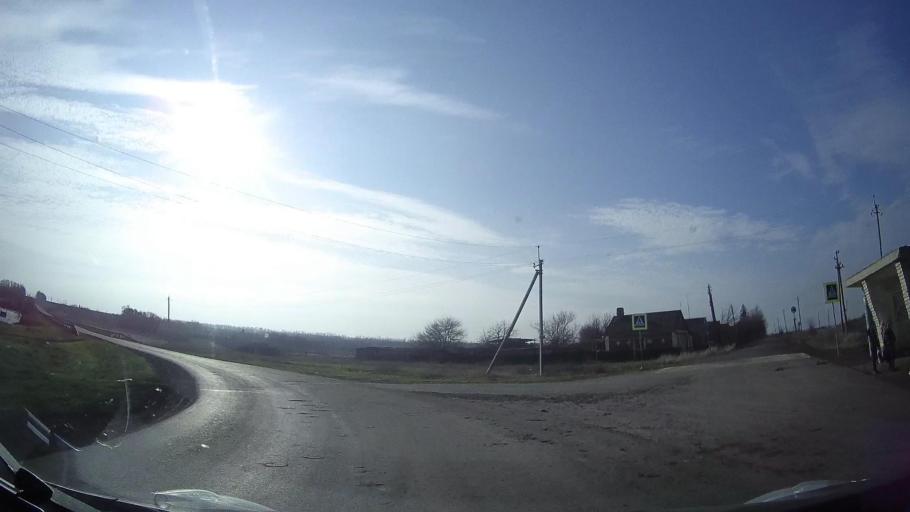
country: RU
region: Rostov
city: Mechetinskaya
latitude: 46.9134
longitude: 40.5355
